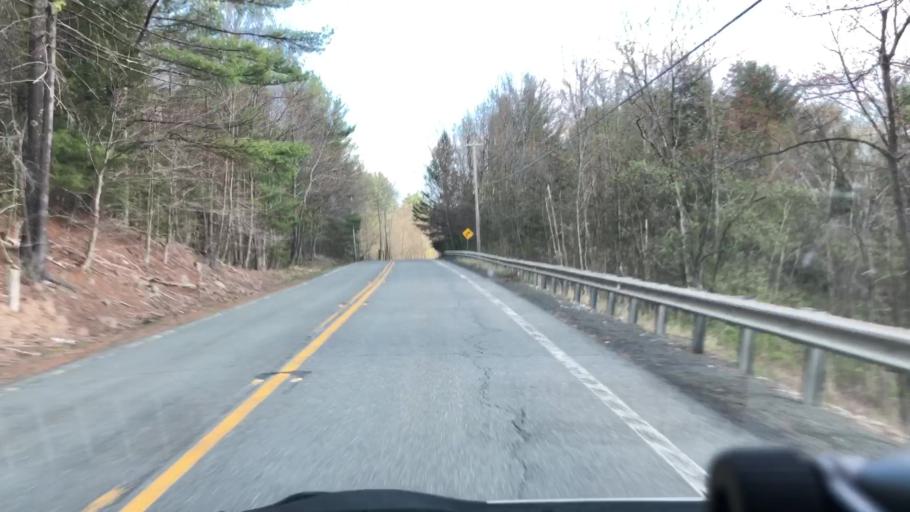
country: US
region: Massachusetts
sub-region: Hampshire County
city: Chesterfield
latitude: 42.3568
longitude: -72.9059
